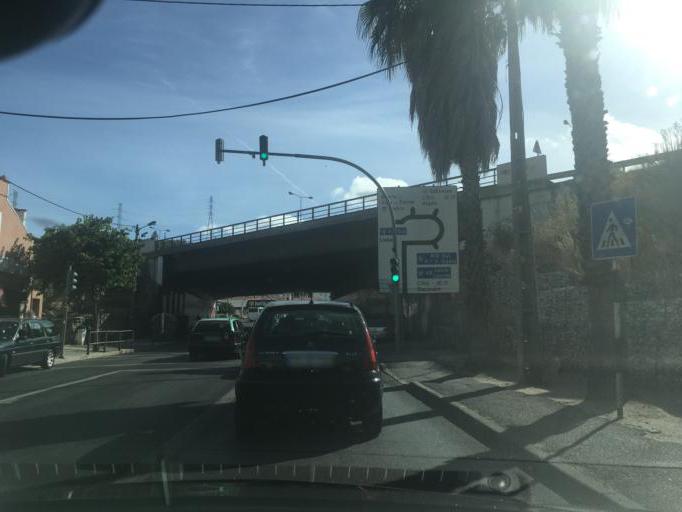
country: PT
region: Lisbon
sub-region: Odivelas
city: Olival do Basto
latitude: 38.7882
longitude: -9.1693
